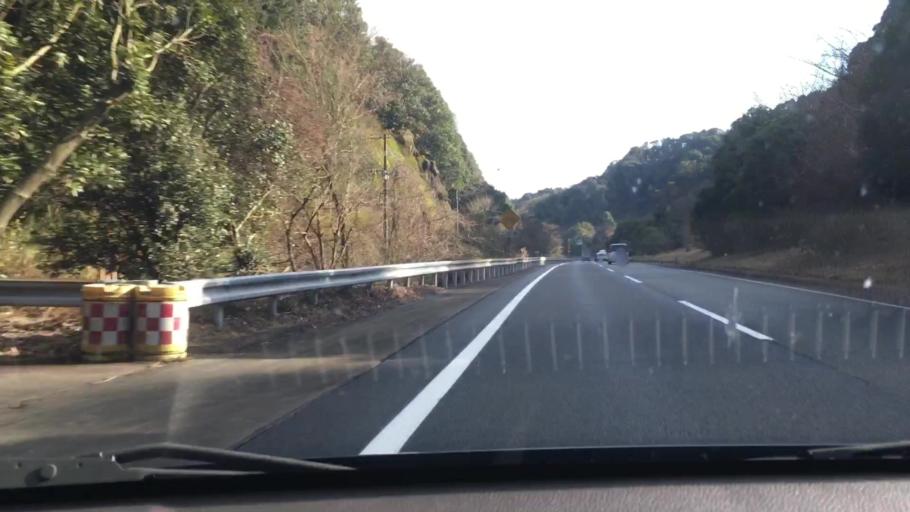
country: JP
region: Kumamoto
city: Hitoyoshi
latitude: 32.2719
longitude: 130.7593
